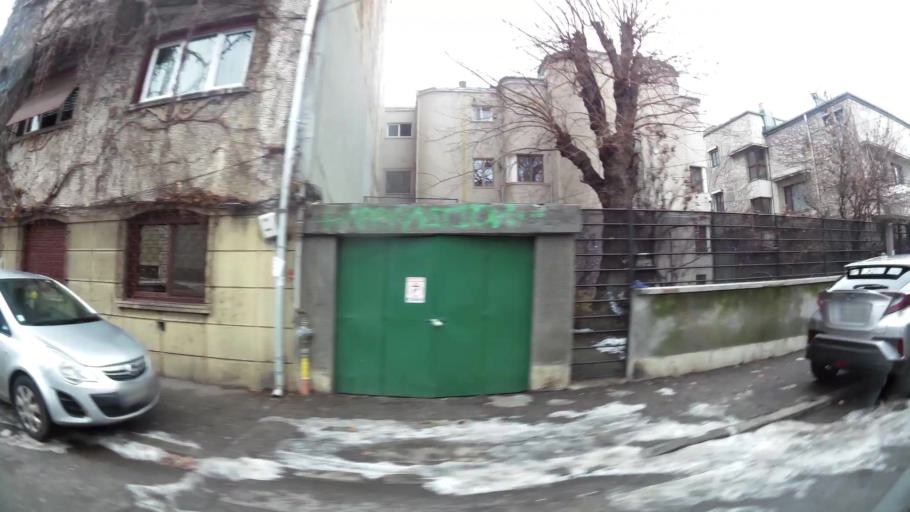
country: RO
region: Bucuresti
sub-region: Municipiul Bucuresti
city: Bucharest
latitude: 44.4364
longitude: 26.1194
